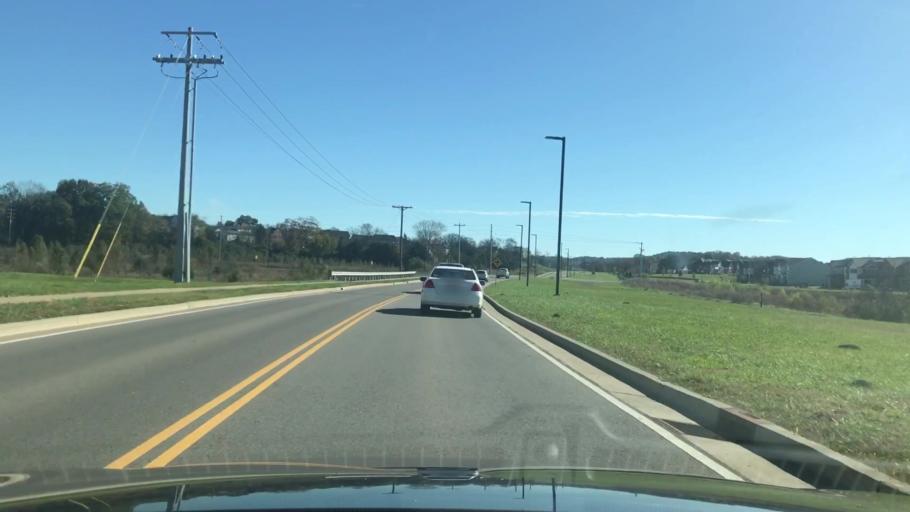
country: US
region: Tennessee
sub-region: Williamson County
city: Franklin
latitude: 35.8875
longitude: -86.8196
